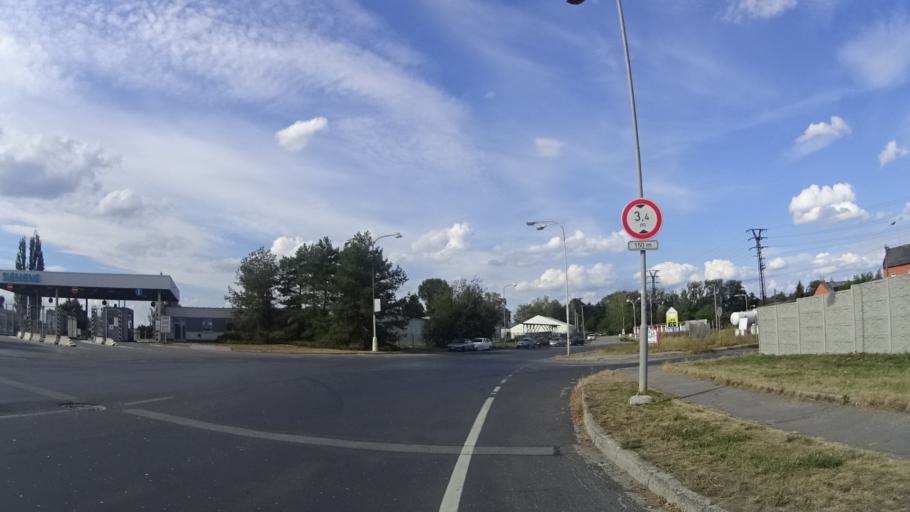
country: CZ
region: Olomoucky
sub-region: Okres Sumperk
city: Mohelnice
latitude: 49.7778
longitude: 16.9399
